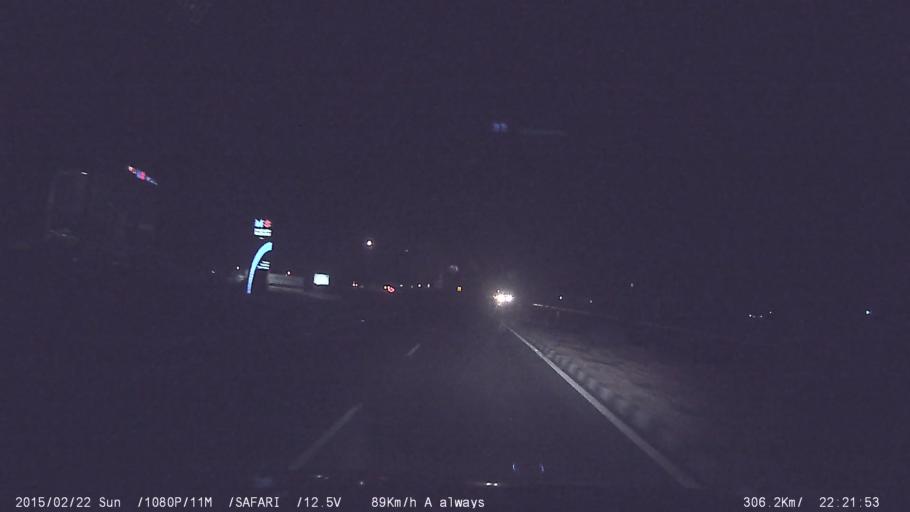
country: IN
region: Tamil Nadu
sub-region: Karur
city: Karur
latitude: 11.0083
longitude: 78.0687
